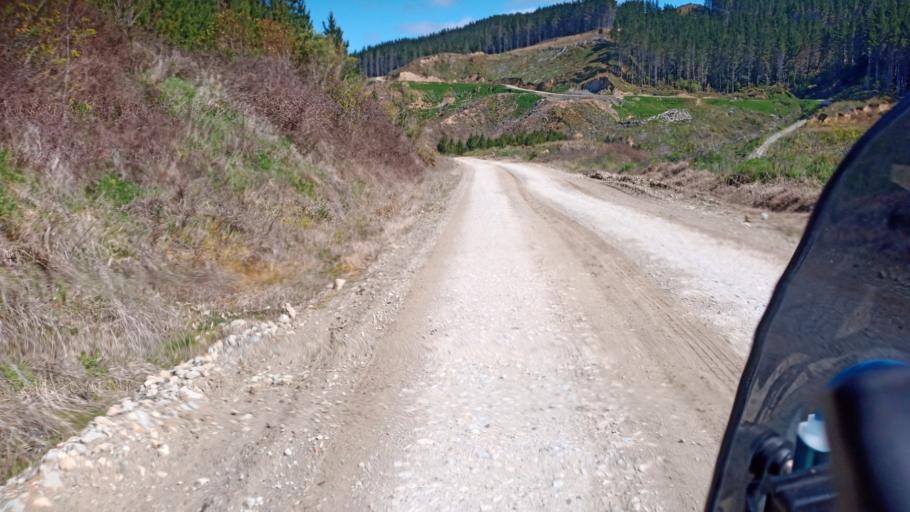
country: NZ
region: Gisborne
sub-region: Gisborne District
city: Gisborne
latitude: -38.8798
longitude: 177.7846
